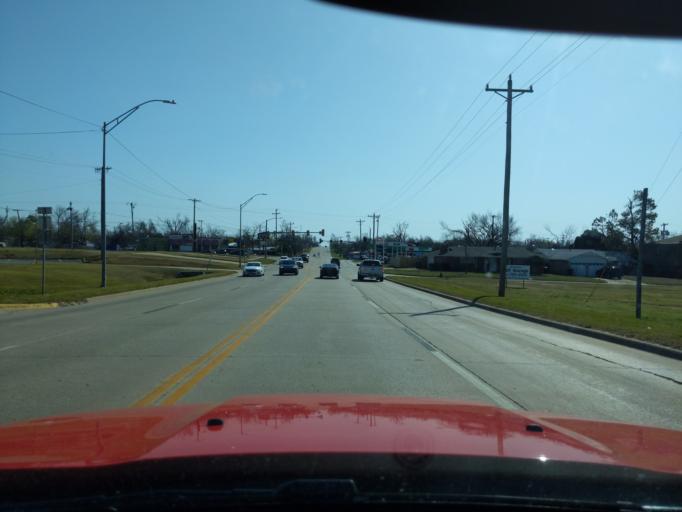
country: US
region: Oklahoma
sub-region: Cleveland County
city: Moore
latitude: 35.3488
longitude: -97.4926
